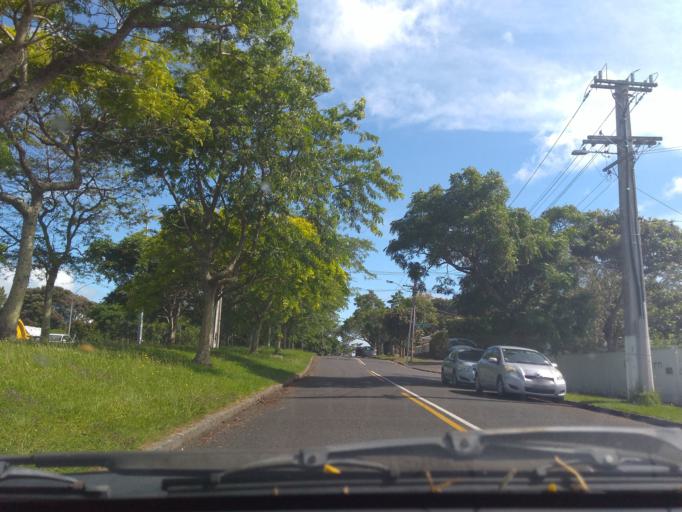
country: NZ
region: Auckland
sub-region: Auckland
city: Auckland
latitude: -36.8748
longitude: 174.7260
